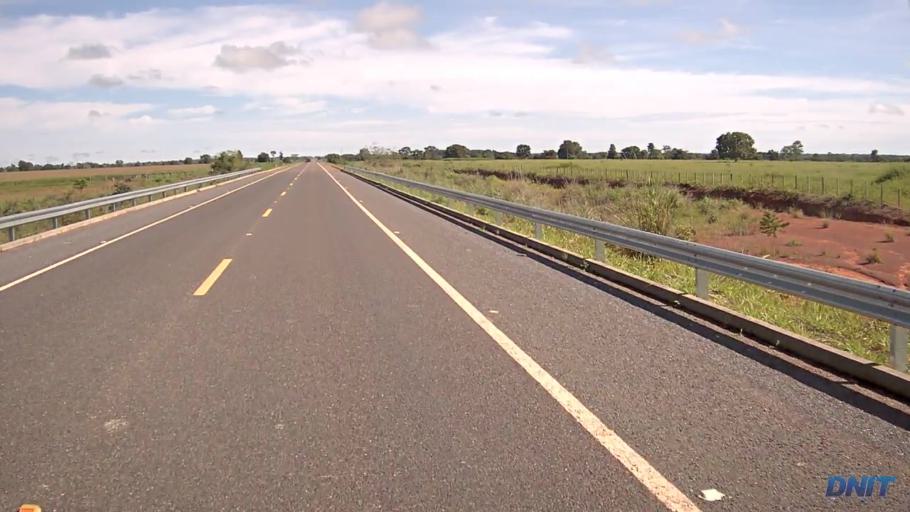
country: BR
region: Goias
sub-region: Sao Miguel Do Araguaia
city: Sao Miguel do Araguaia
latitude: -13.3948
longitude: -50.1368
